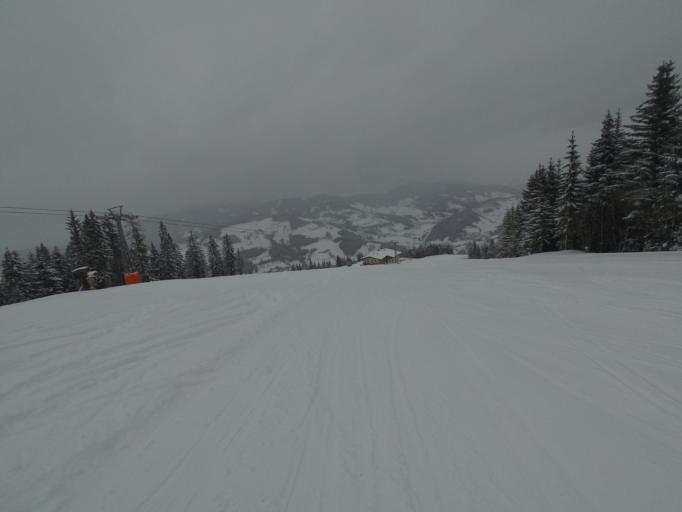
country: AT
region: Salzburg
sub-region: Politischer Bezirk Sankt Johann im Pongau
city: Wagrain
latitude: 47.3163
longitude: 13.2851
